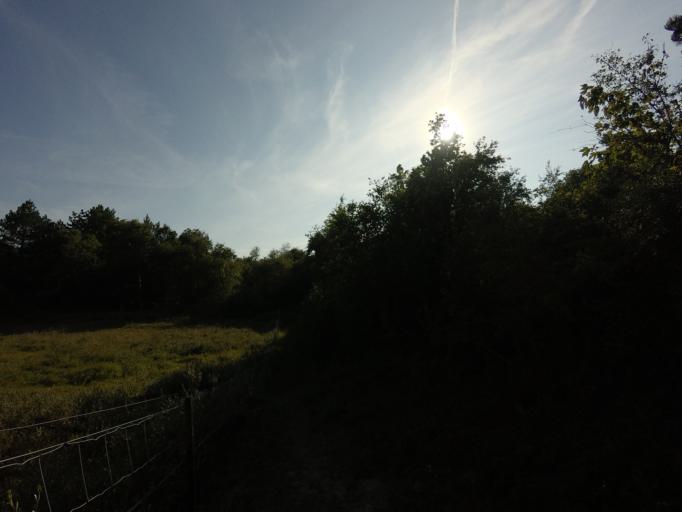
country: NL
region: Friesland
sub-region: Gemeente Schiermonnikoog
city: Schiermonnikoog
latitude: 53.4899
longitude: 6.1741
